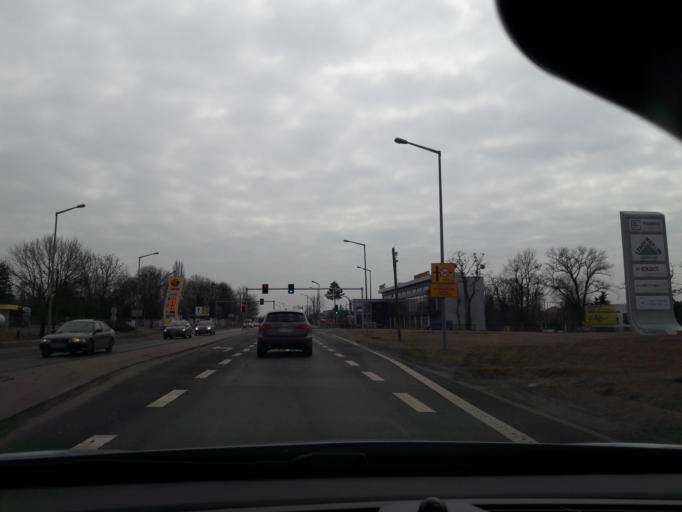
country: PL
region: Greater Poland Voivodeship
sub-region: Powiat poznanski
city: Zlotniki
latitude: 52.4868
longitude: 16.8532
